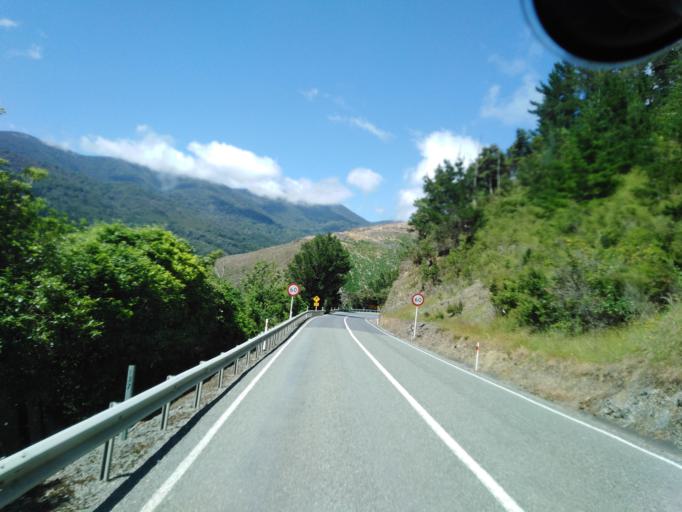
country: NZ
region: Nelson
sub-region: Nelson City
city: Nelson
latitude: -41.2279
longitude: 173.4242
